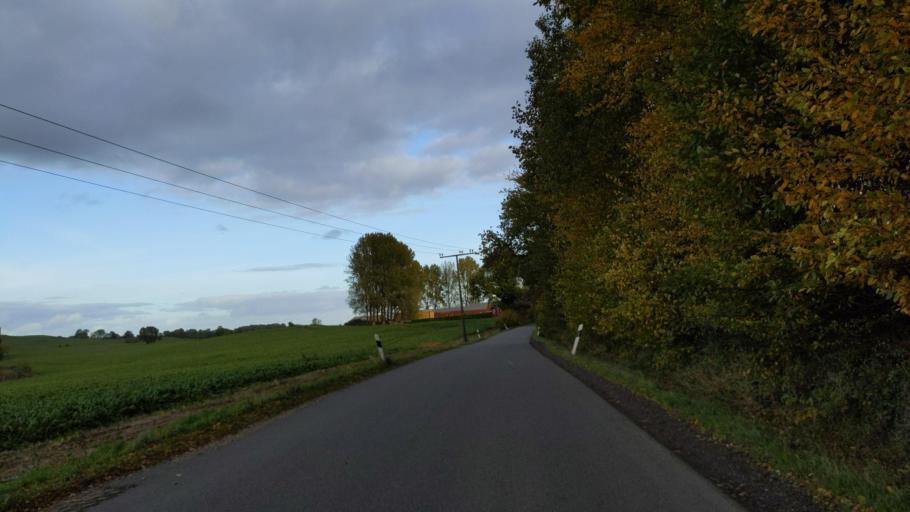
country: DE
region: Schleswig-Holstein
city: Susel
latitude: 54.1017
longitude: 10.7298
